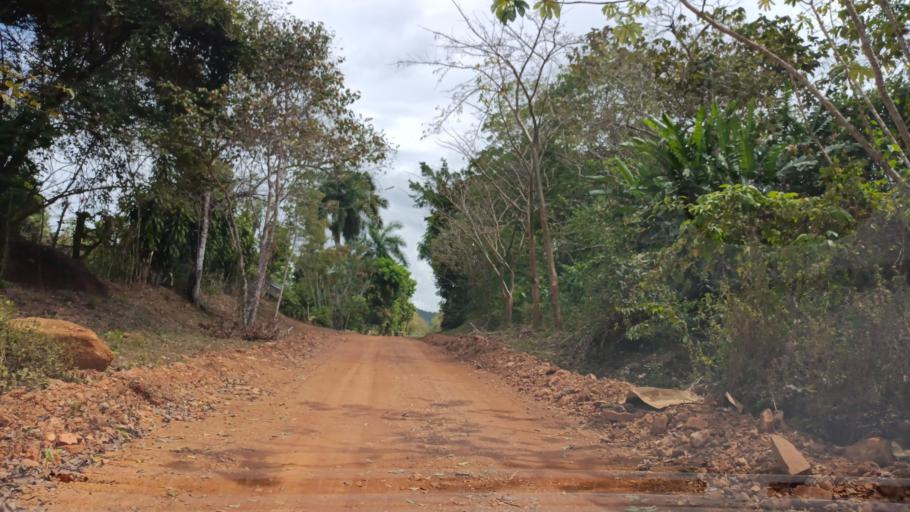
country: PA
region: Panama
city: La Cabima
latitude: 9.1301
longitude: -79.5001
